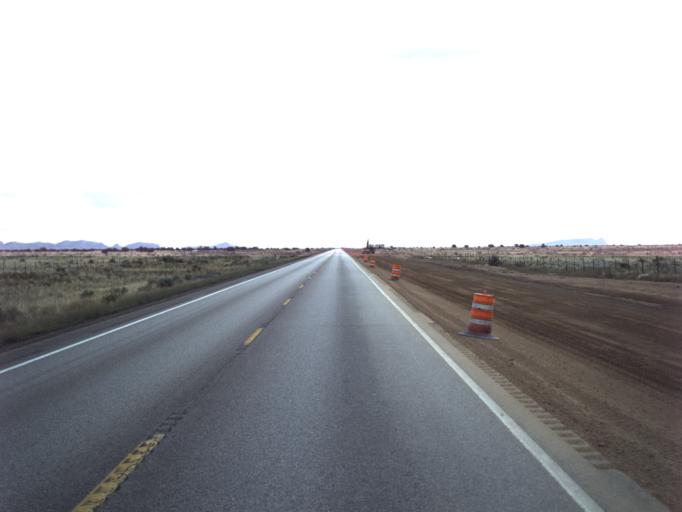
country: US
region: Utah
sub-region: Carbon County
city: East Carbon City
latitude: 39.4356
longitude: -110.4578
